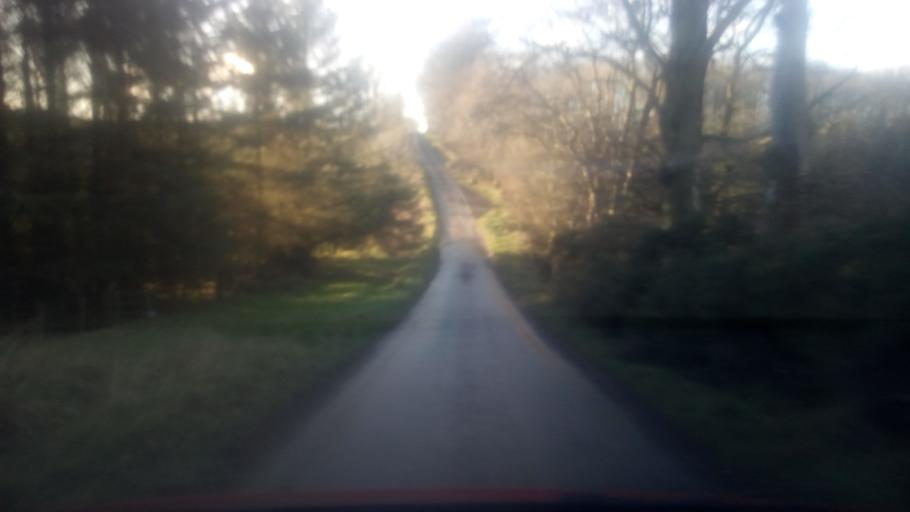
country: GB
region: Scotland
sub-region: The Scottish Borders
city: Jedburgh
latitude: 55.4688
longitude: -2.4387
